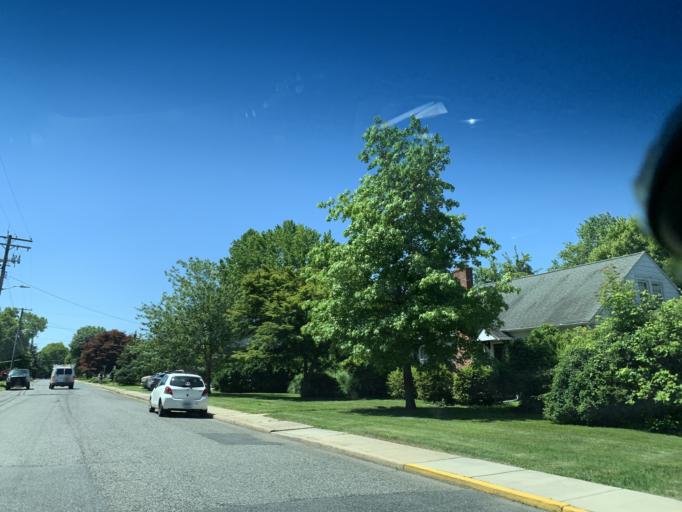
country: US
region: Maryland
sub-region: Harford County
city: Havre de Grace
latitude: 39.5413
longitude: -76.0951
